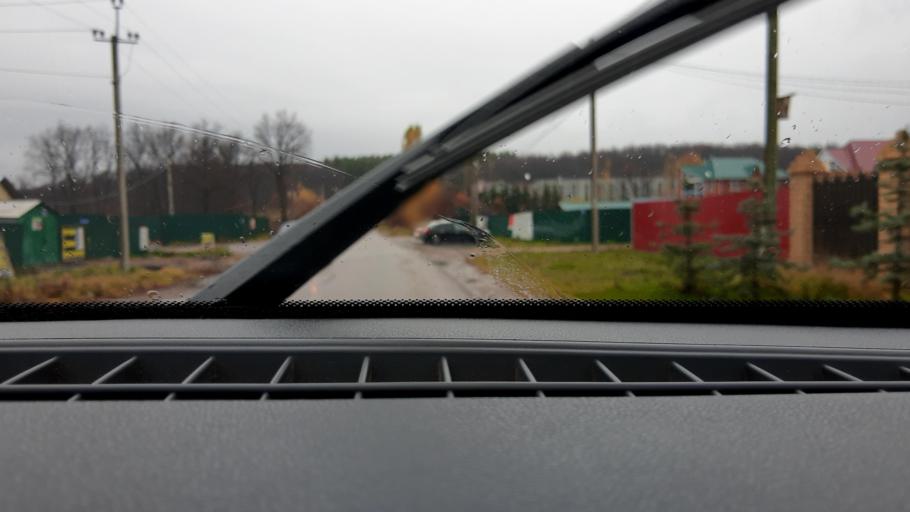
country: RU
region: Bashkortostan
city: Mikhaylovka
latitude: 54.8041
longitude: 55.8788
